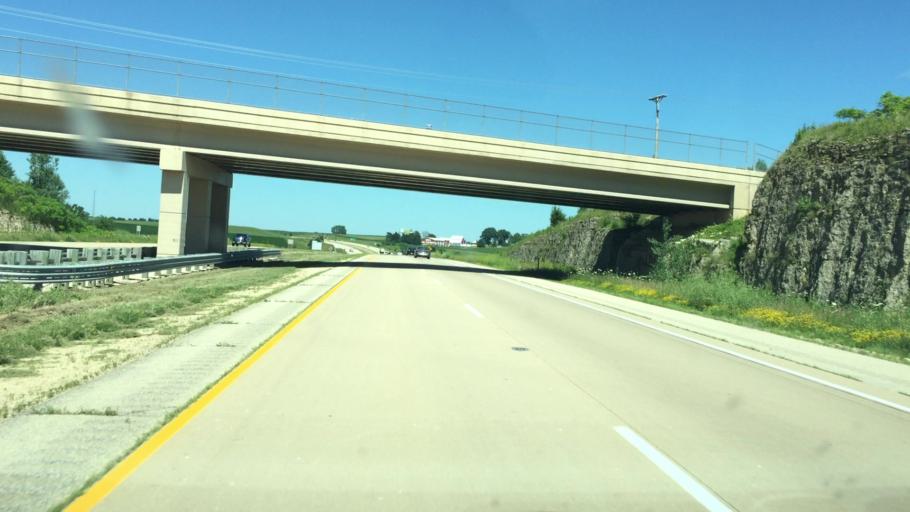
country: US
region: Wisconsin
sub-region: Grant County
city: Platteville
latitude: 42.7446
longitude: -90.3389
